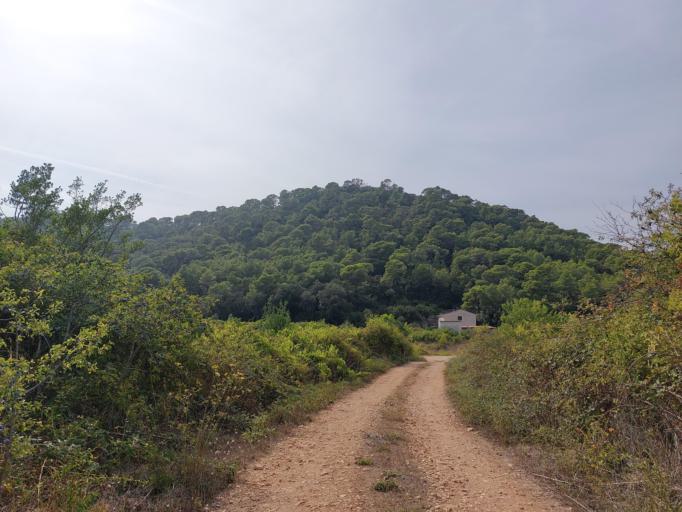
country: HR
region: Dubrovacko-Neretvanska
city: Smokvica
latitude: 42.7497
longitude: 16.8371
